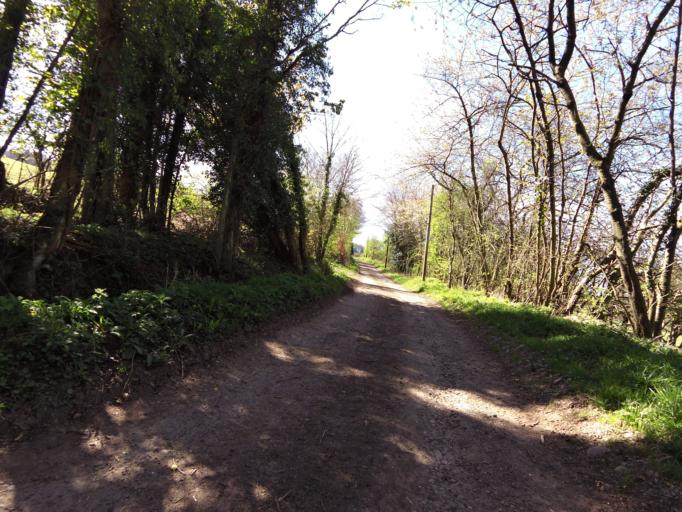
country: GB
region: Scotland
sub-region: Fife
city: Cupar
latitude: 56.3945
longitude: -3.0721
